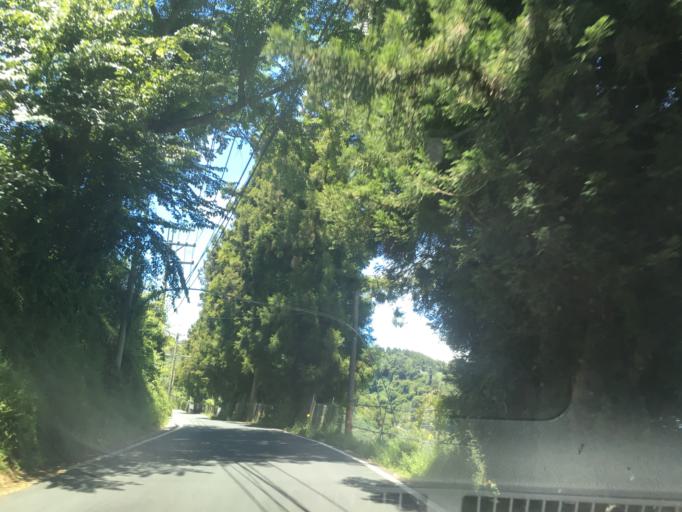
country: TW
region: Taiwan
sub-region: Nantou
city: Puli
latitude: 24.2551
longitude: 121.2587
